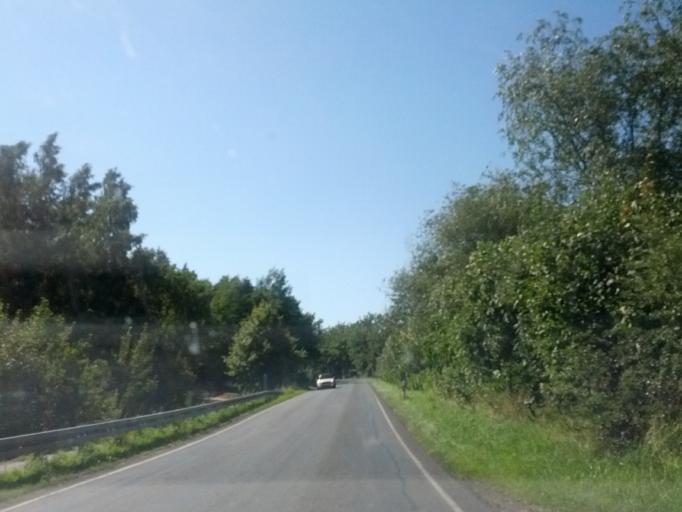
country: DE
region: Mecklenburg-Vorpommern
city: Bergen auf Ruegen
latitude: 54.4340
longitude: 13.4337
